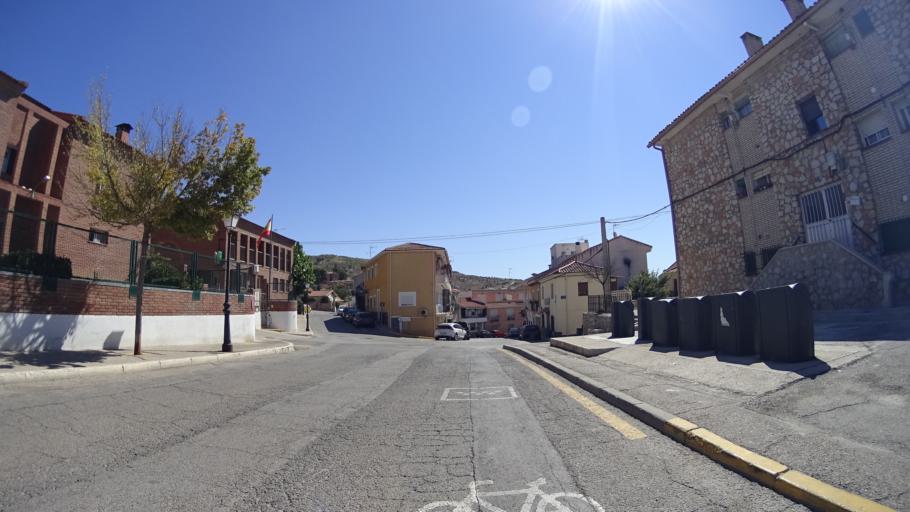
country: ES
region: Madrid
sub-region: Provincia de Madrid
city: Morata de Tajuna
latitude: 40.2323
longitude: -3.4378
